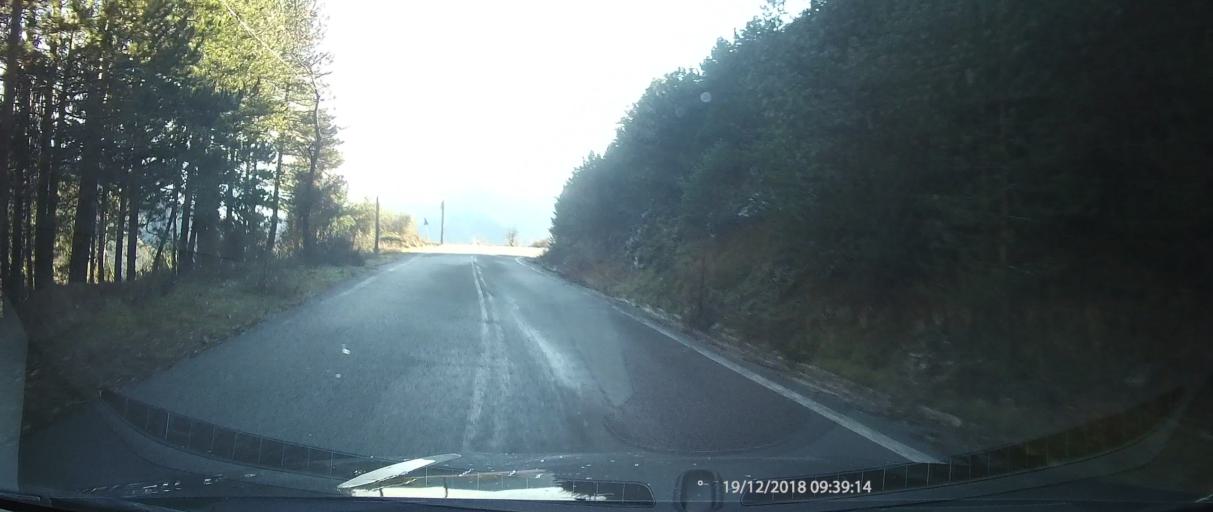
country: GR
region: Peloponnese
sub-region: Nomos Lakonias
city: Magoula
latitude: 37.0796
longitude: 22.2706
